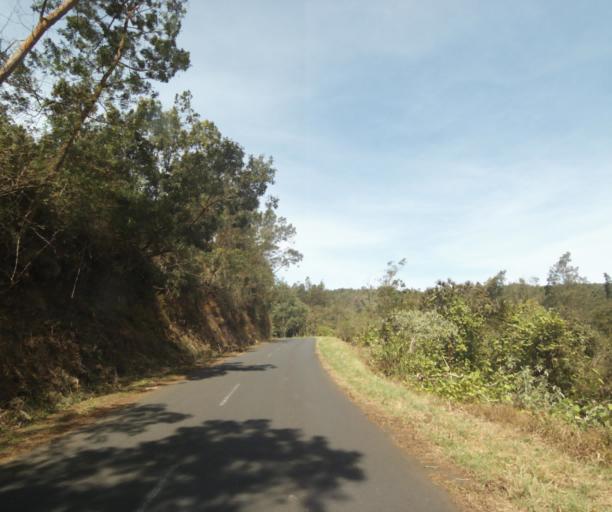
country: RE
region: Reunion
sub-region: Reunion
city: Trois-Bassins
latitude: -21.0492
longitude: 55.3450
